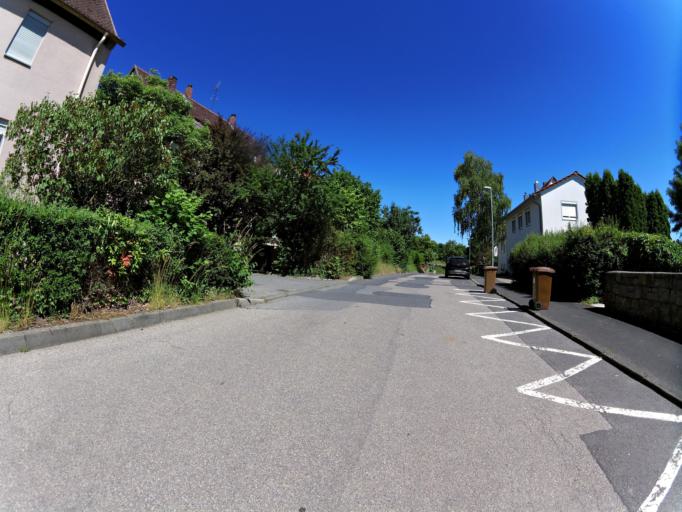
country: DE
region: Bavaria
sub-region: Regierungsbezirk Unterfranken
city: Ochsenfurt
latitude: 49.6705
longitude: 10.0609
